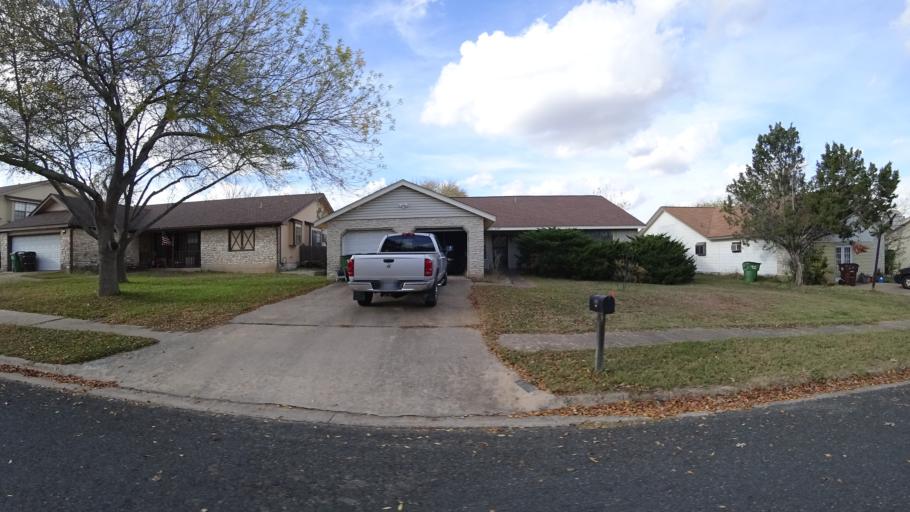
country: US
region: Texas
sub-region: Williamson County
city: Brushy Creek
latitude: 30.5092
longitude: -97.7255
